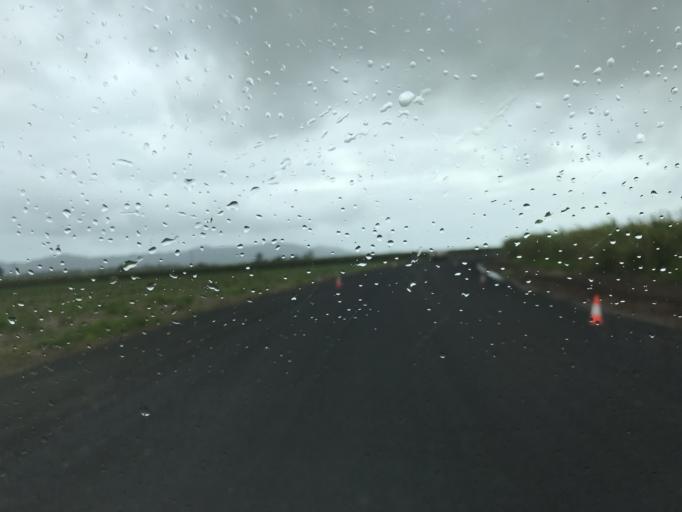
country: AU
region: Queensland
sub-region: Cassowary Coast
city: Innisfail
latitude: -17.5001
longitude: 145.9852
